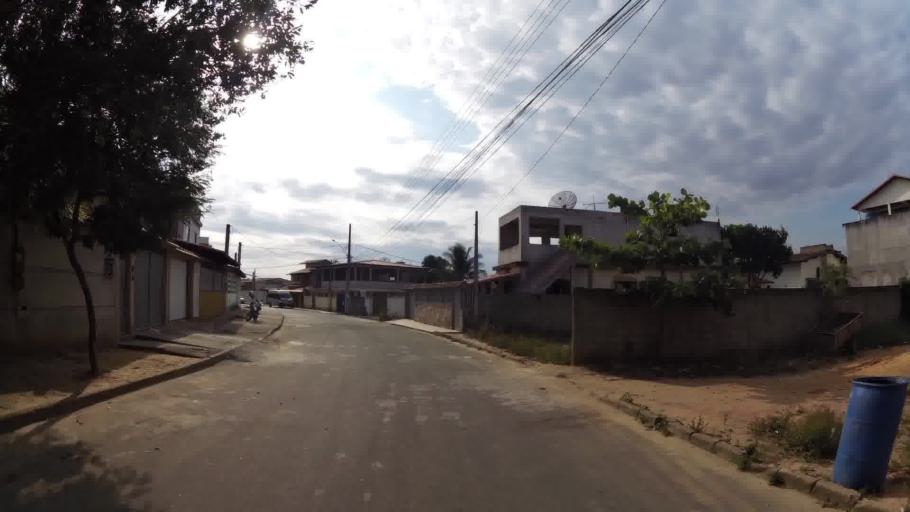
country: BR
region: Espirito Santo
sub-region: Itapemirim
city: Itapemirim
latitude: -21.0112
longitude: -40.8302
